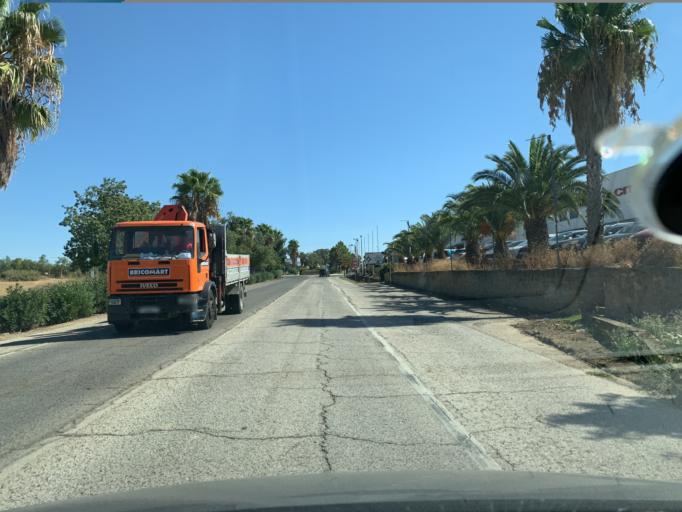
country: ES
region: Andalusia
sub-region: Provincia de Sevilla
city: Carmona
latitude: 37.4686
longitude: -5.6632
